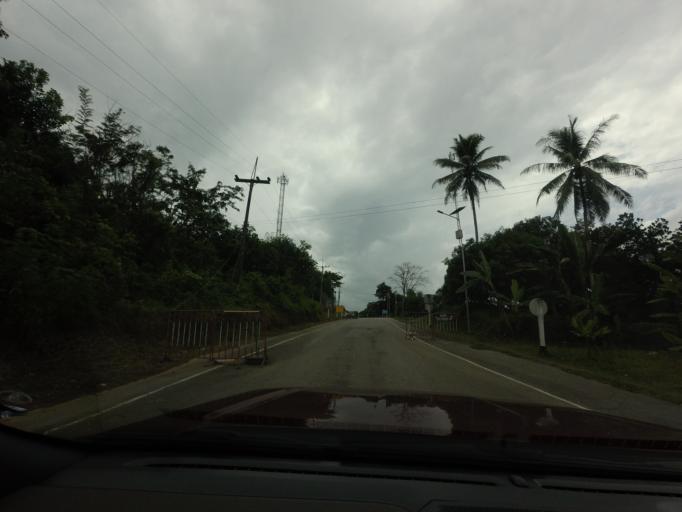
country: TH
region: Narathiwat
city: Sukhirin
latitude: 5.9779
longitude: 101.7073
